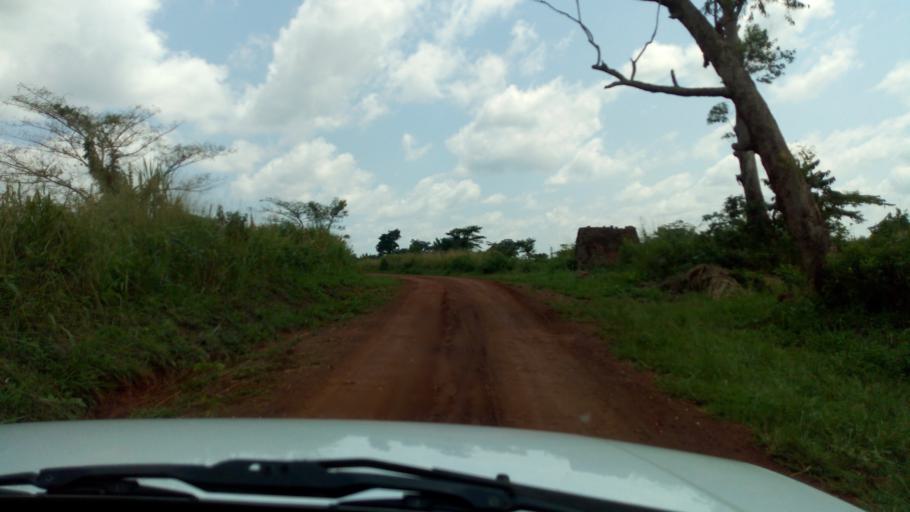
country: UG
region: Western Region
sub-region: Masindi District
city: Masindi
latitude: 1.7576
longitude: 31.8582
